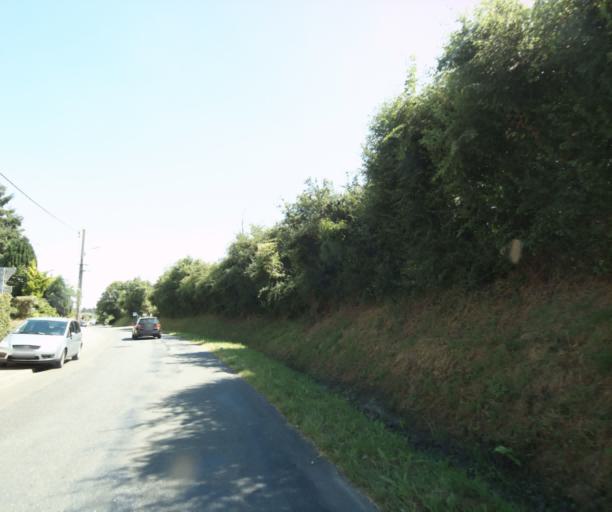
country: FR
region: Pays de la Loire
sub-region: Departement de la Mayenne
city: Change
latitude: 48.0796
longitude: -0.7939
